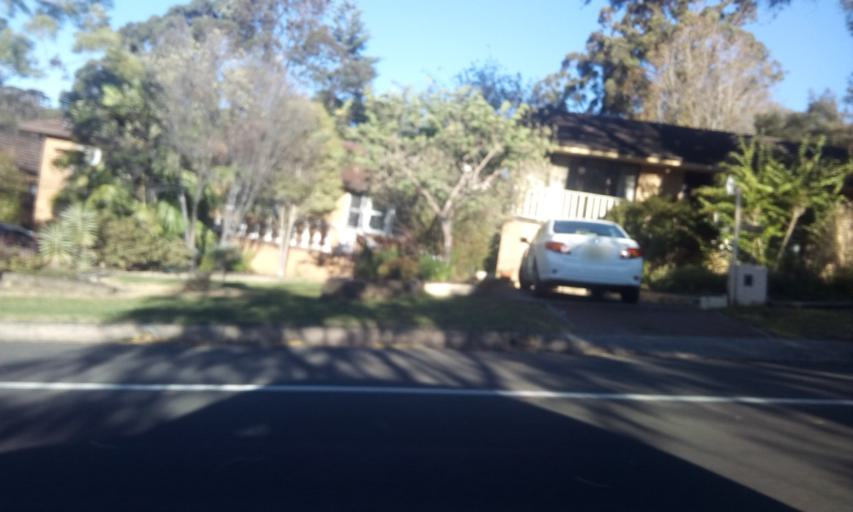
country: AU
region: New South Wales
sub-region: Wollongong
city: Mount Keira
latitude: -34.4247
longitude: 150.8474
